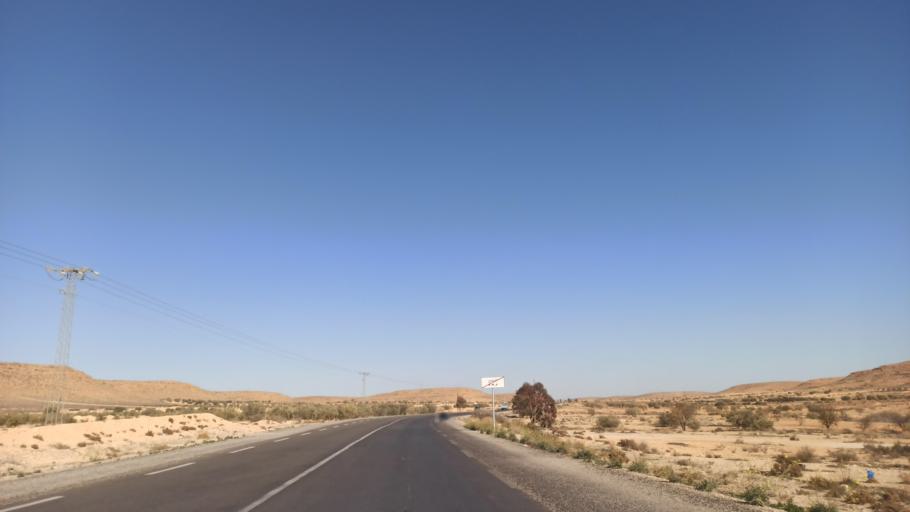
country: TN
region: Sidi Bu Zayd
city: Bi'r al Hufayy
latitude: 34.7072
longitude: 9.0467
